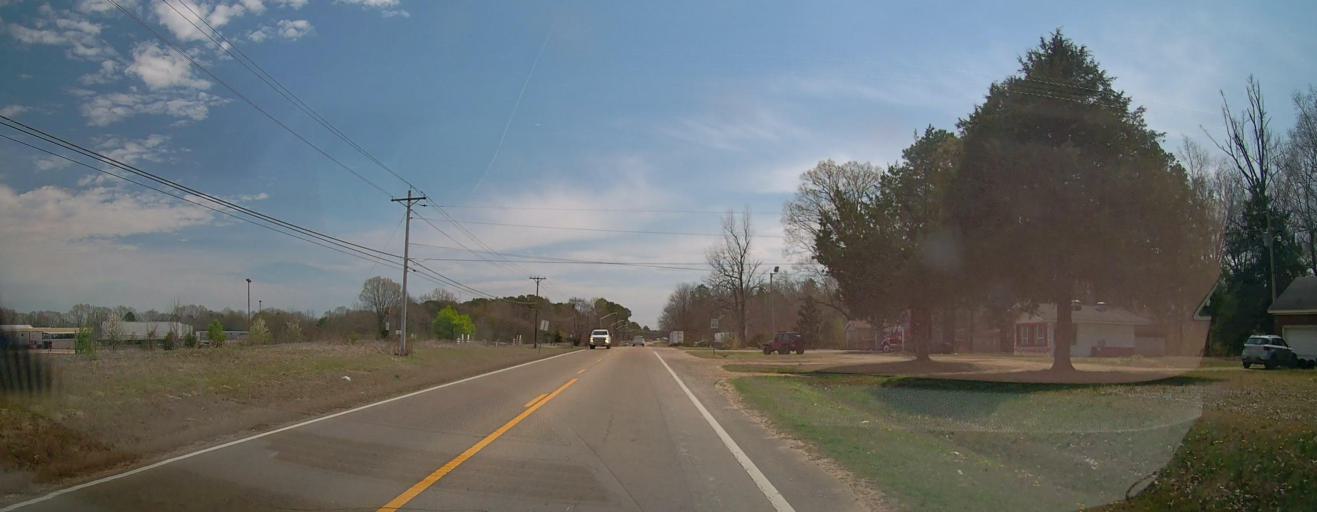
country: US
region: Mississippi
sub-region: Union County
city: New Albany
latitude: 34.5158
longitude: -89.0457
